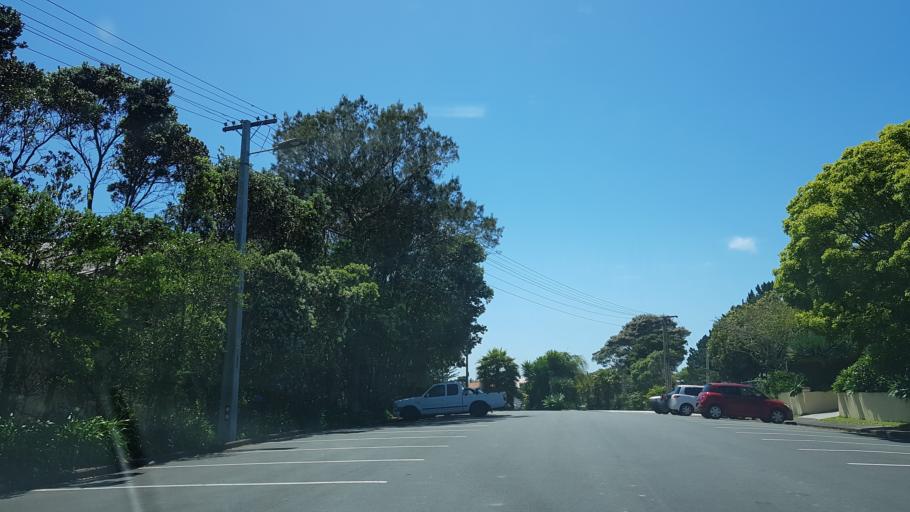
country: NZ
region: Auckland
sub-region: Auckland
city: North Shore
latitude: -36.8086
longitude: 174.7215
